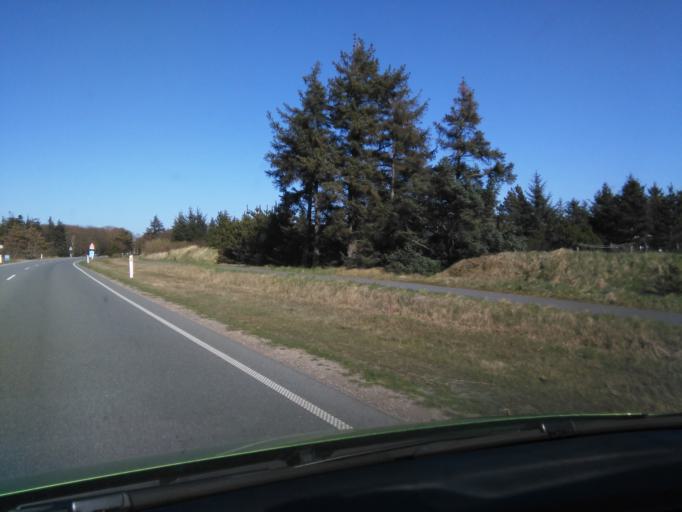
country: DK
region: South Denmark
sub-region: Varde Kommune
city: Oksbol
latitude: 55.5626
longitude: 8.1694
